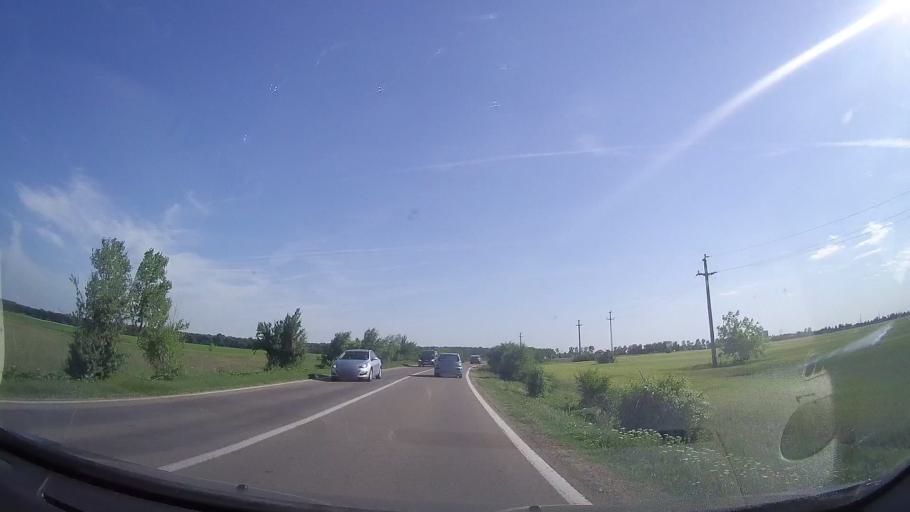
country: RO
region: Prahova
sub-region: Comuna Berceni
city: Corlatesti
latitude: 44.9200
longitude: 26.1014
